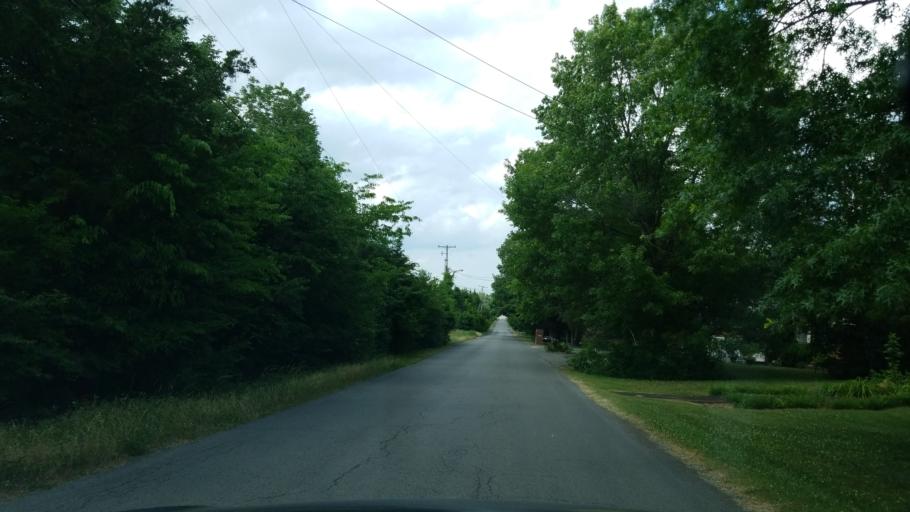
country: US
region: Tennessee
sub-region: Rutherford County
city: La Vergne
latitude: 36.0833
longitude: -86.6182
